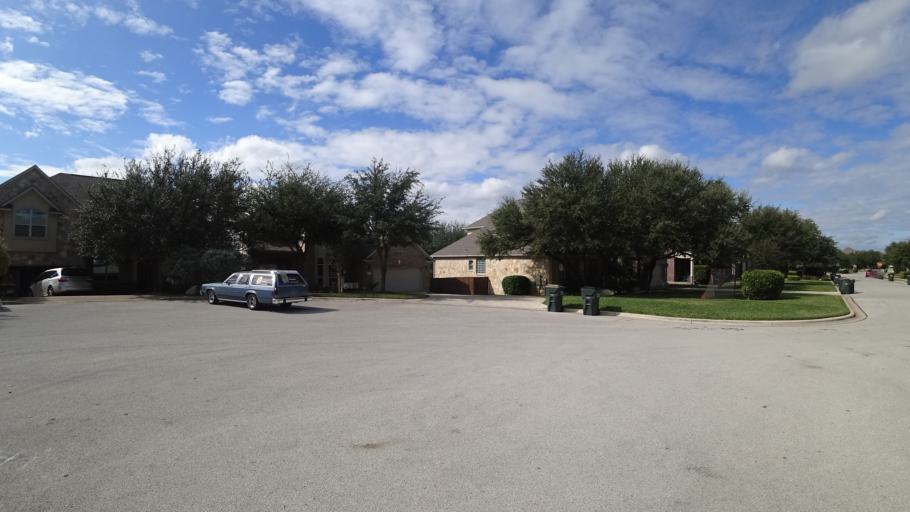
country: US
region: Texas
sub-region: Travis County
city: Hudson Bend
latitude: 30.3669
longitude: -97.9062
